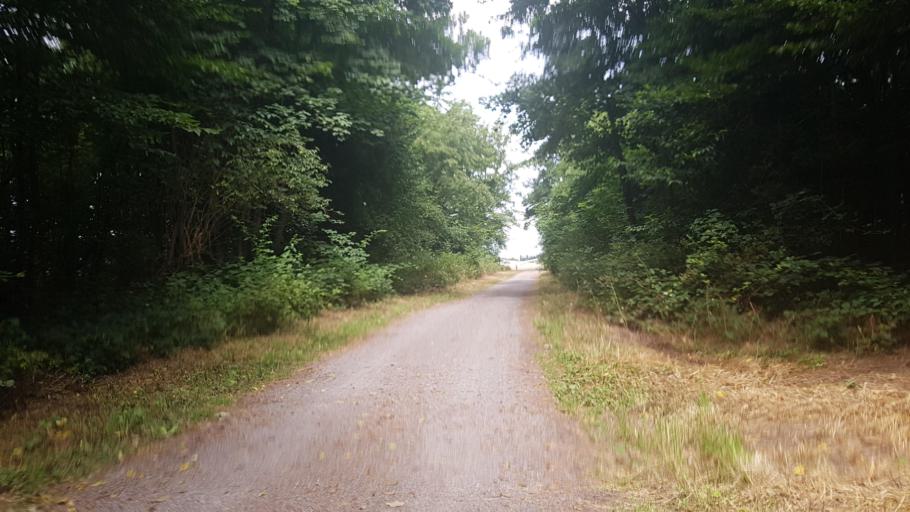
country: DE
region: Baden-Wuerttemberg
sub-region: Karlsruhe Region
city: Rheinstetten
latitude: 48.9715
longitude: 8.3433
